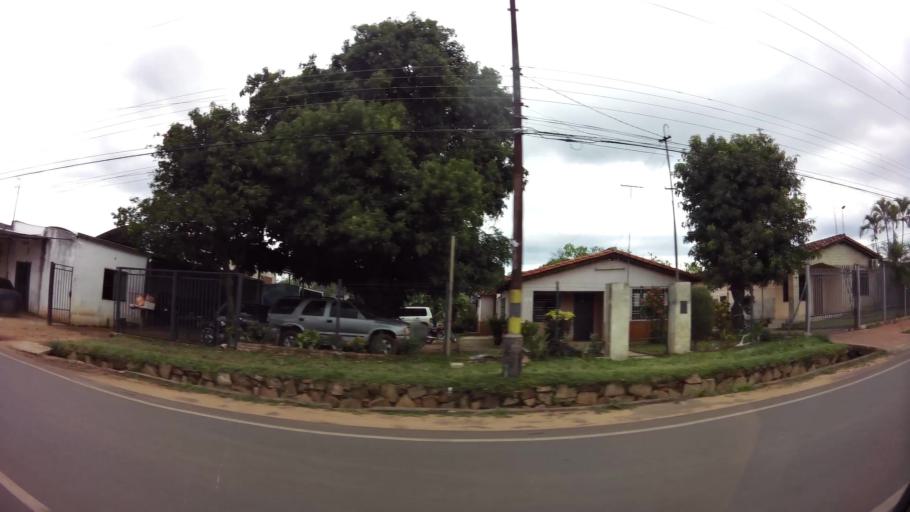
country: PY
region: Central
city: San Lorenzo
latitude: -25.2887
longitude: -57.4870
